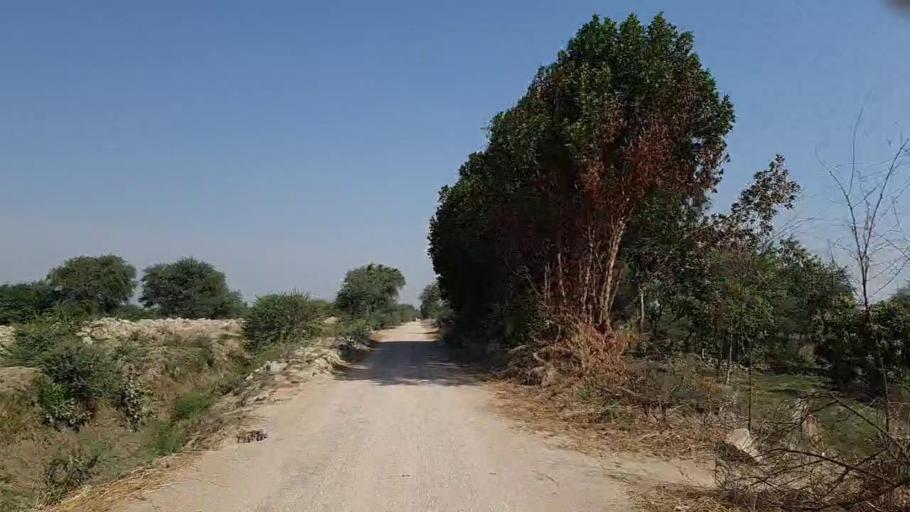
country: PK
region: Sindh
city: Mirpur Batoro
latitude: 24.6876
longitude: 68.2577
